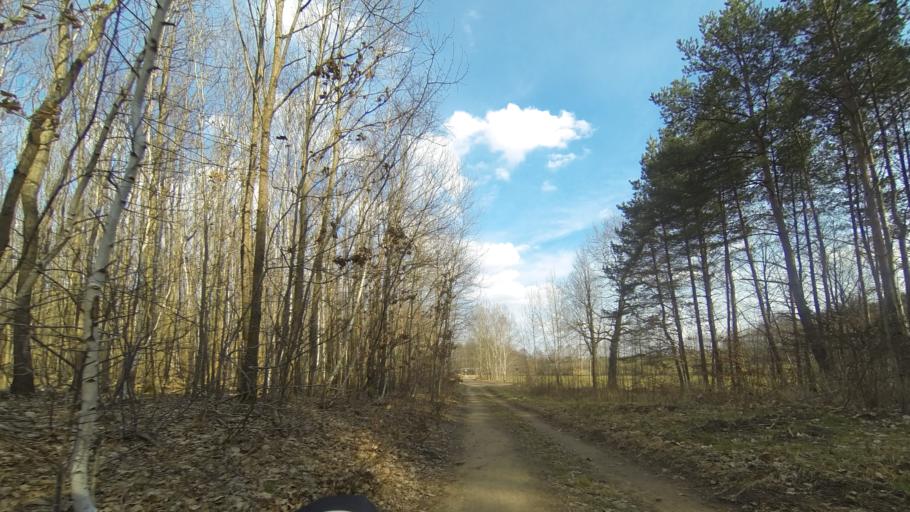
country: DE
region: Saxony
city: Moritzburg
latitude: 51.1486
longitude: 13.6454
